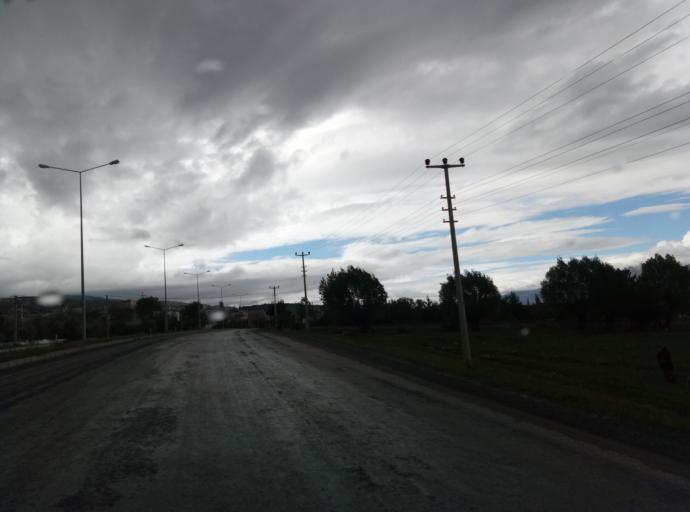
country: TR
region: Sivas
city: Susehri
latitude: 40.1691
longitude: 38.0969
